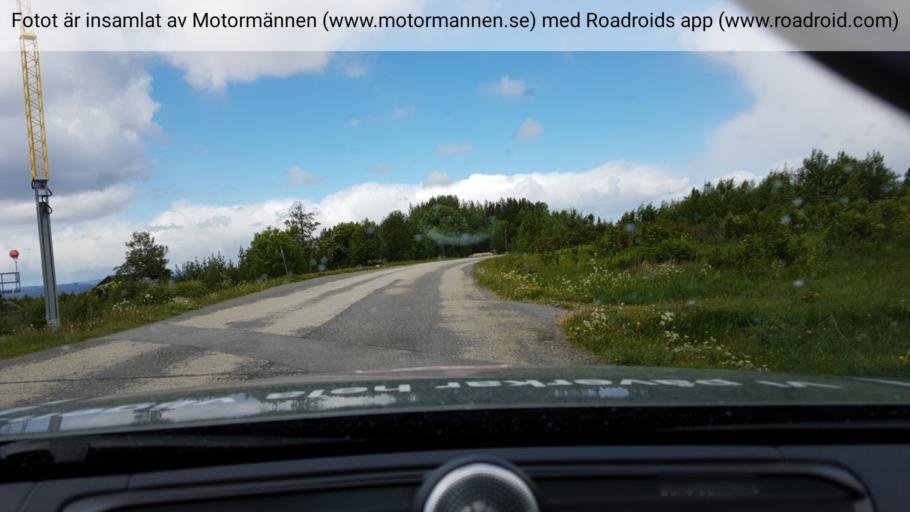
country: SE
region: Jaemtland
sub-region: Krokoms Kommun
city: Krokom
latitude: 63.2009
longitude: 14.4689
